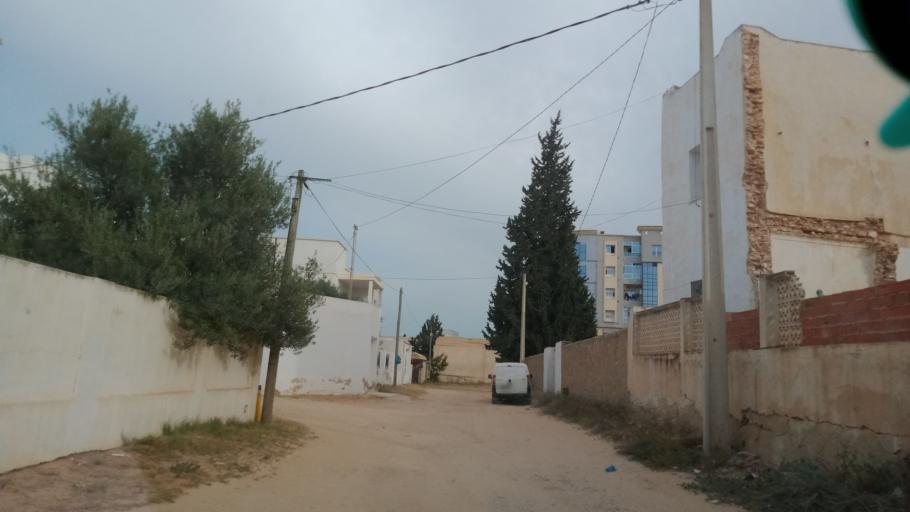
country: TN
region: Safaqis
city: Al Qarmadah
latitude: 34.8002
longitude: 10.7573
